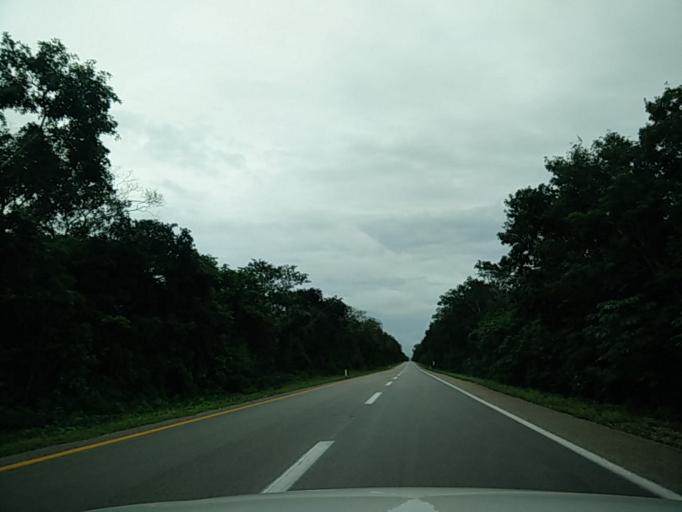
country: MX
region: Quintana Roo
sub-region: Lazaro Cardenas
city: Ignacio Zaragoza
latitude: 20.8918
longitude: -87.5215
